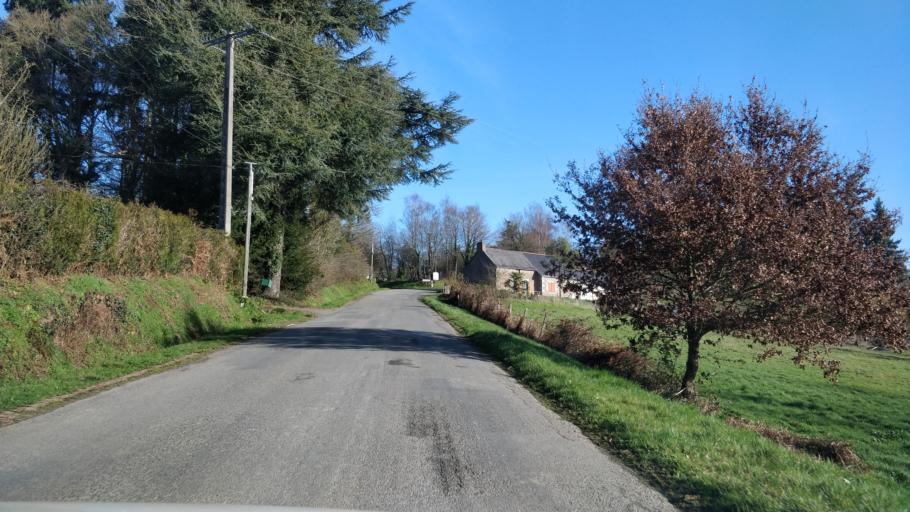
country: FR
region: Brittany
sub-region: Departement d'Ille-et-Vilaine
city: Sens-de-Bretagne
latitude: 48.3486
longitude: -1.4888
